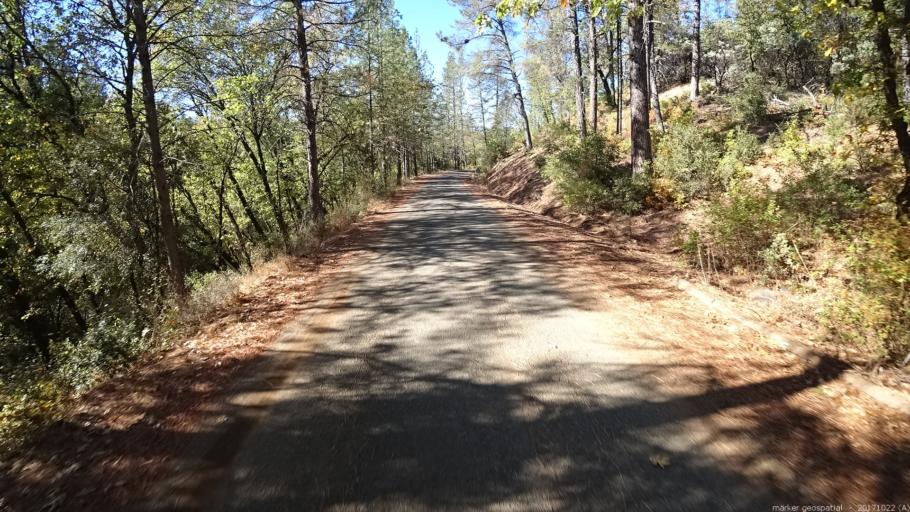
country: US
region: California
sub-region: Shasta County
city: Shasta Lake
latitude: 40.8775
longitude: -122.3664
